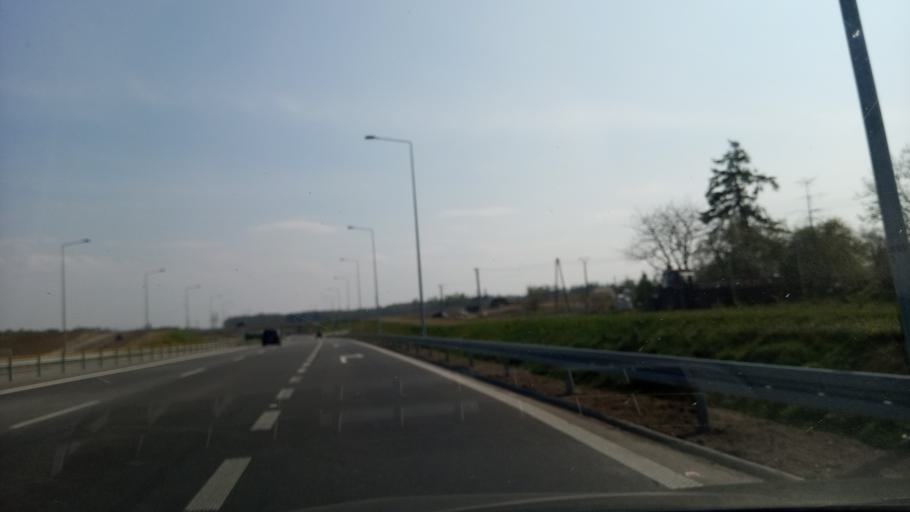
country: PL
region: West Pomeranian Voivodeship
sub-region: Powiat szczecinecki
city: Szczecinek
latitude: 53.6939
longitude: 16.7303
